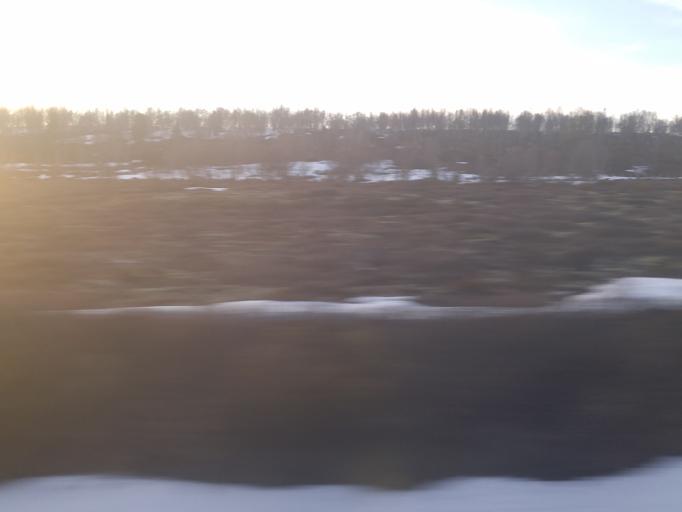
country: NO
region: Oppland
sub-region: Dovre
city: Dovre
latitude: 62.1057
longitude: 9.2490
